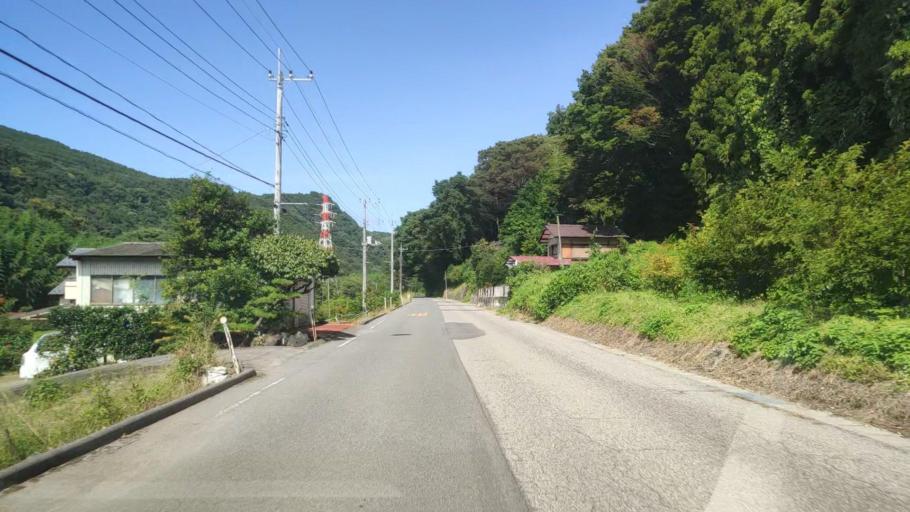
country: JP
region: Gunma
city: Numata
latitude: 36.5908
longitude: 139.0548
